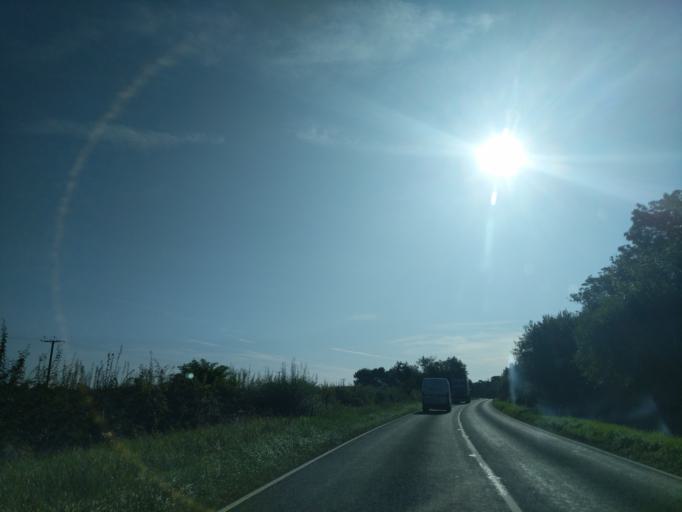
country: GB
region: England
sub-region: District of Rutland
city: Clipsham
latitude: 52.8041
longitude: -0.5984
